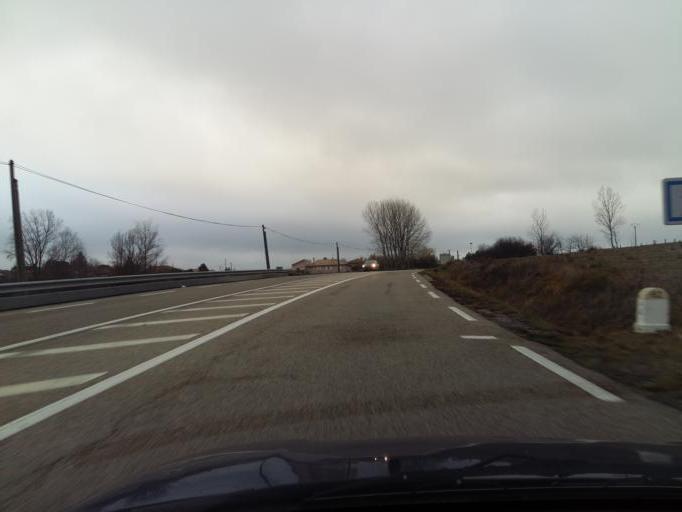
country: FR
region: Rhone-Alpes
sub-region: Departement de l'Ardeche
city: Saint-Cyr
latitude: 45.2477
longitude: 4.7465
